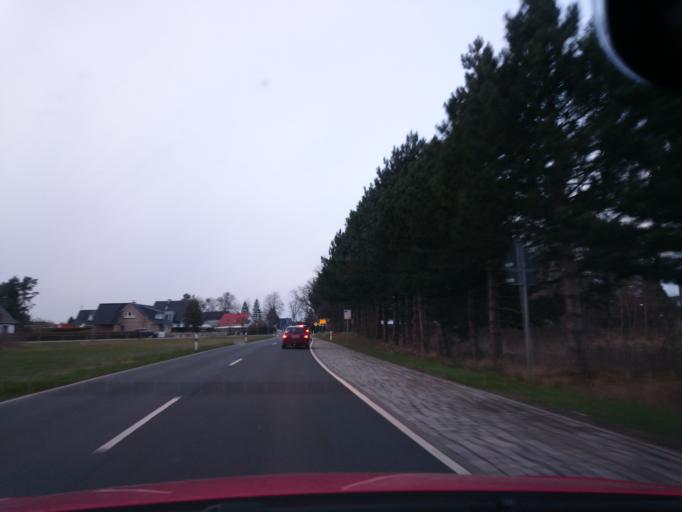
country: DE
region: Mecklenburg-Vorpommern
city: Barth
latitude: 54.3759
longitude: 12.6735
